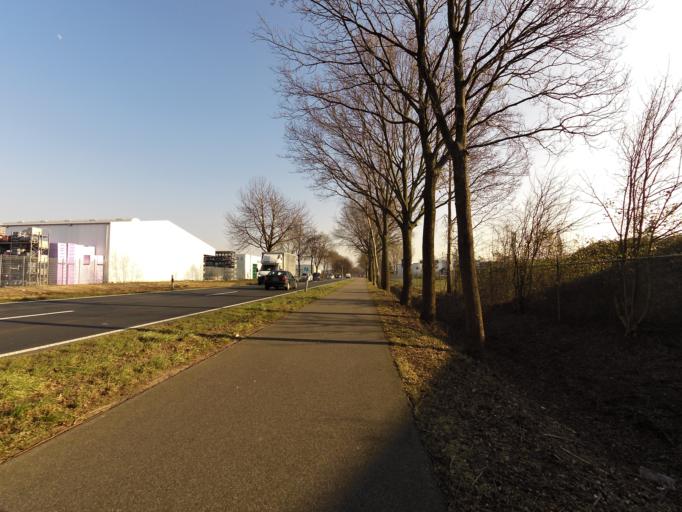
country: DE
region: North Rhine-Westphalia
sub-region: Regierungsbezirk Dusseldorf
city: Emmerich
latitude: 51.8456
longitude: 6.2707
